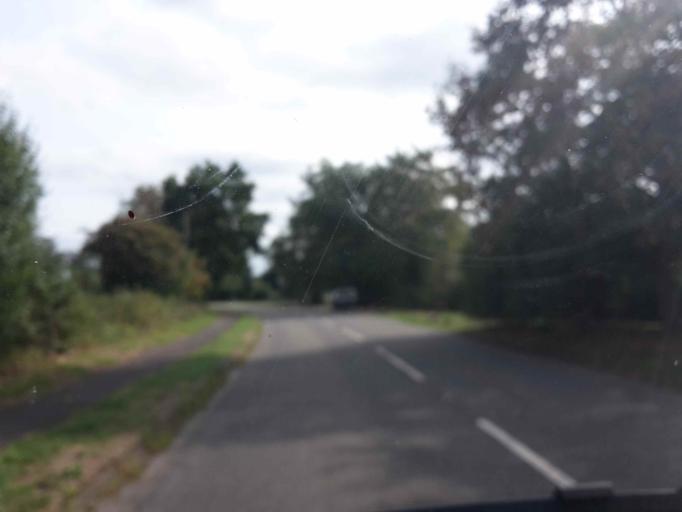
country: GB
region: England
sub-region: Wokingham
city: Twyford
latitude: 51.4628
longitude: -0.8603
